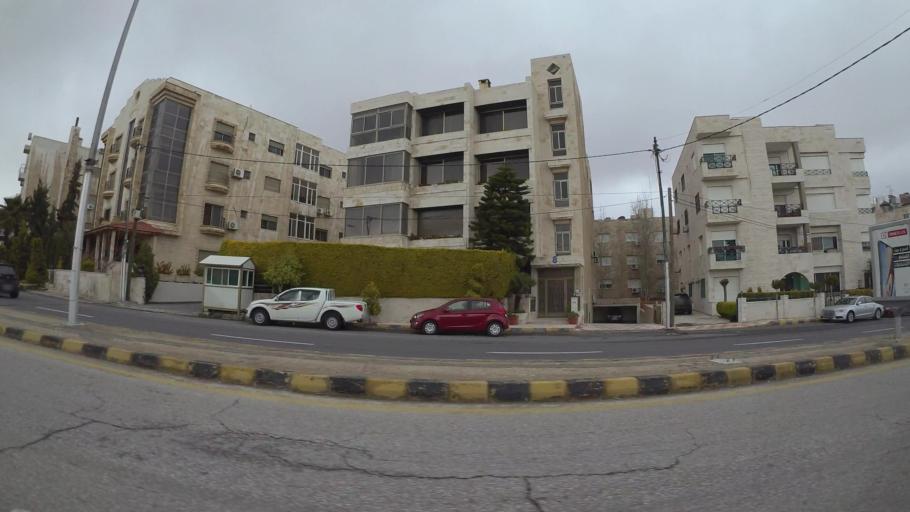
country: JO
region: Amman
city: Al Bunayyat ash Shamaliyah
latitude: 31.9468
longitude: 35.8810
